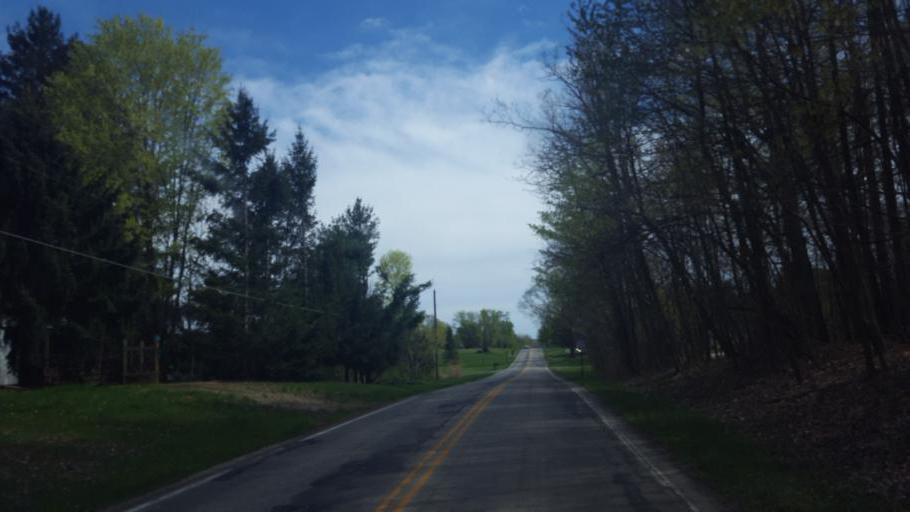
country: US
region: Ohio
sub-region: Richland County
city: Ontario
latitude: 40.8355
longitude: -82.5999
